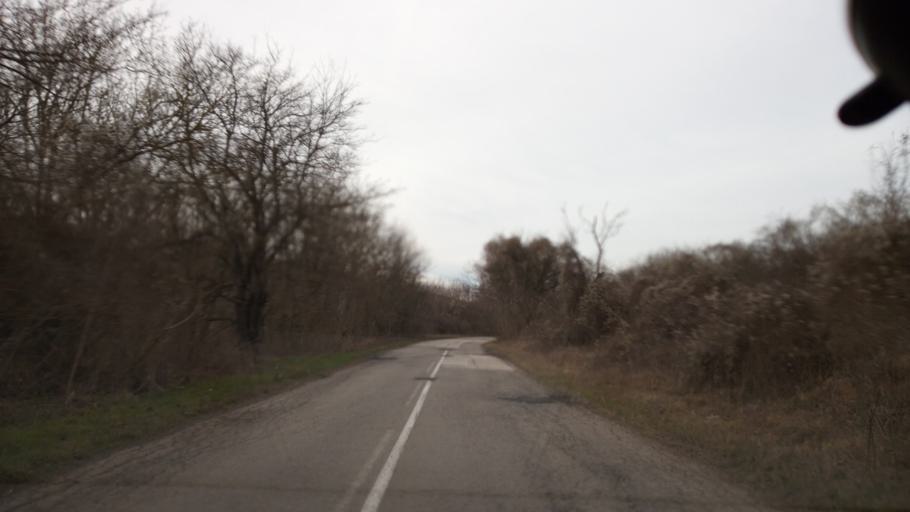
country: BG
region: Pleven
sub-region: Obshtina Belene
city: Belene
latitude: 43.6133
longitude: 25.0229
